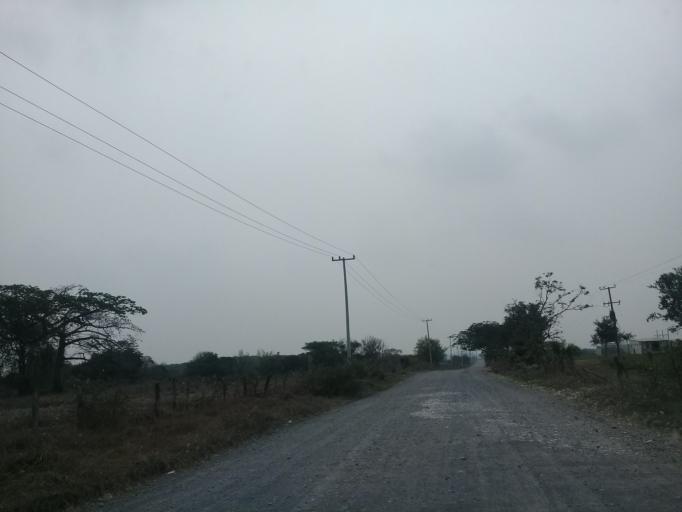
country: MX
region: Veracruz
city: Jamapa
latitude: 18.9114
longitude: -96.2004
